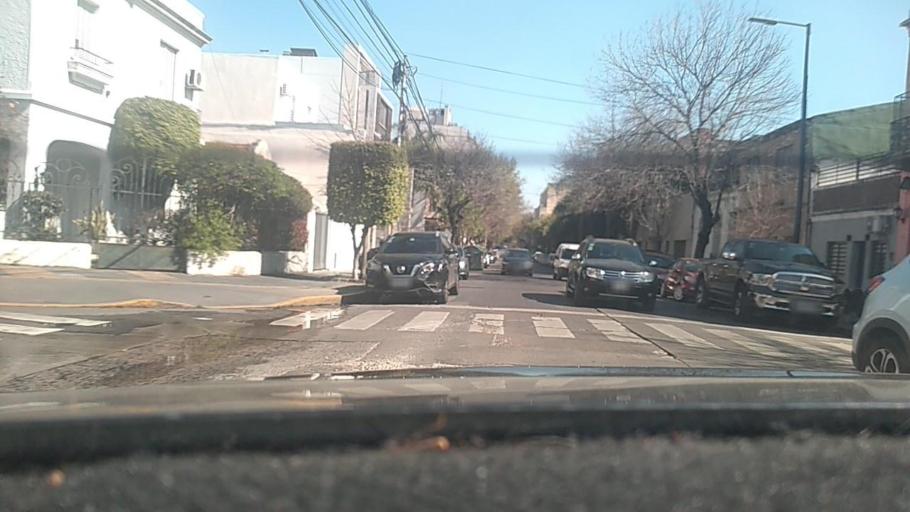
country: AR
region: Buenos Aires F.D.
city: Villa Santa Rita
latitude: -34.6041
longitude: -58.4892
